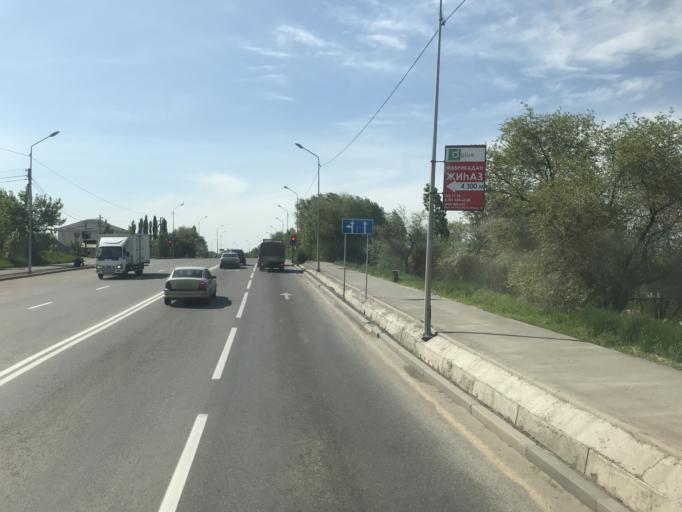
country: KZ
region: Almaty Oblysy
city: Burunday
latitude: 43.3108
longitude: 76.8674
